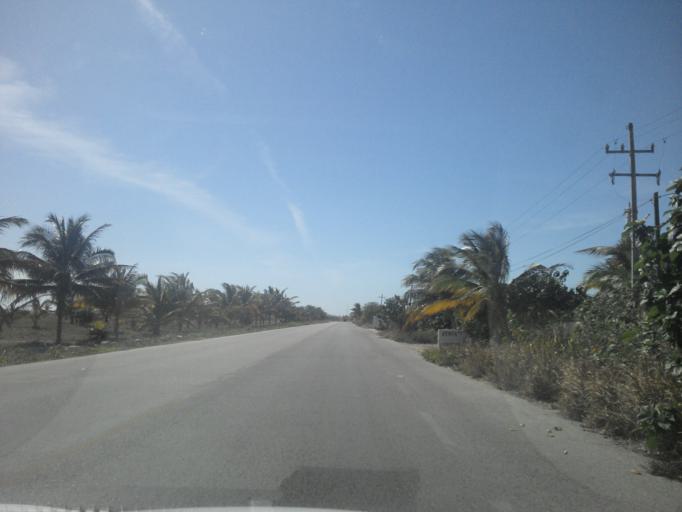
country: MX
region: Yucatan
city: Telchac Puerto
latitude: 21.3317
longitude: -89.3711
